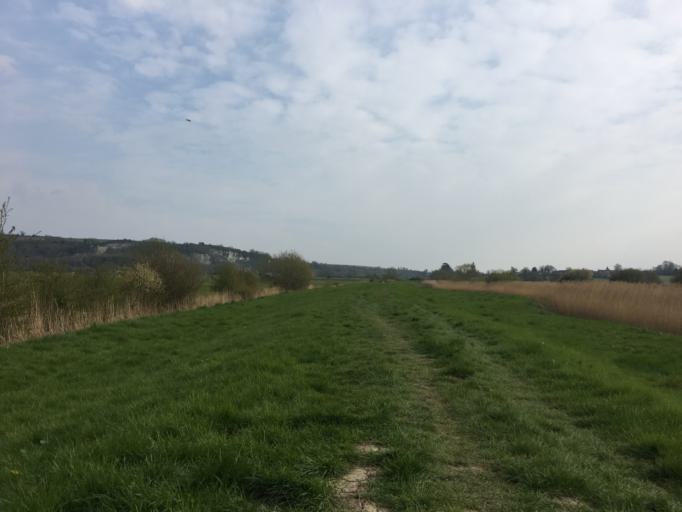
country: GB
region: England
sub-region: West Sussex
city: Arundel
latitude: 50.9027
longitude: -0.5538
